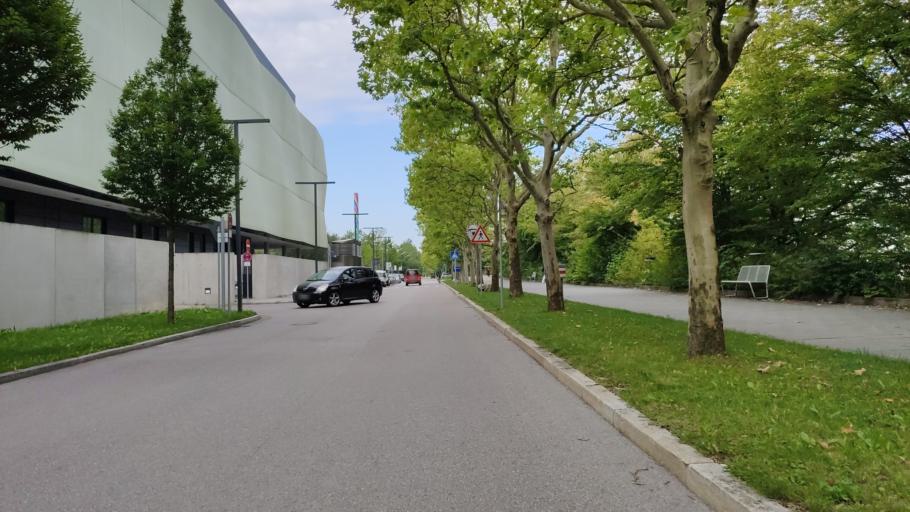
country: DE
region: Bavaria
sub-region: Upper Bavaria
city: Neuried
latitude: 48.1125
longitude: 11.4688
